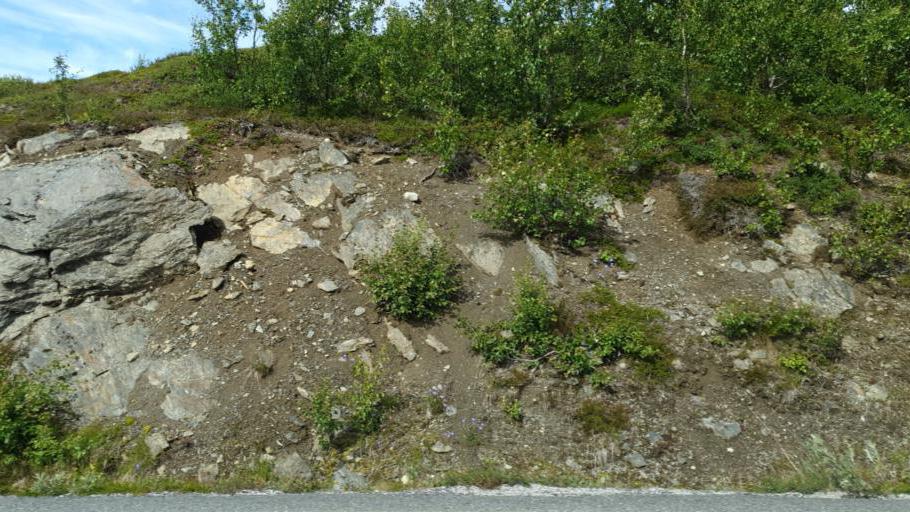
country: NO
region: Oppland
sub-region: Oystre Slidre
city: Heggenes
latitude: 61.5172
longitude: 8.8620
